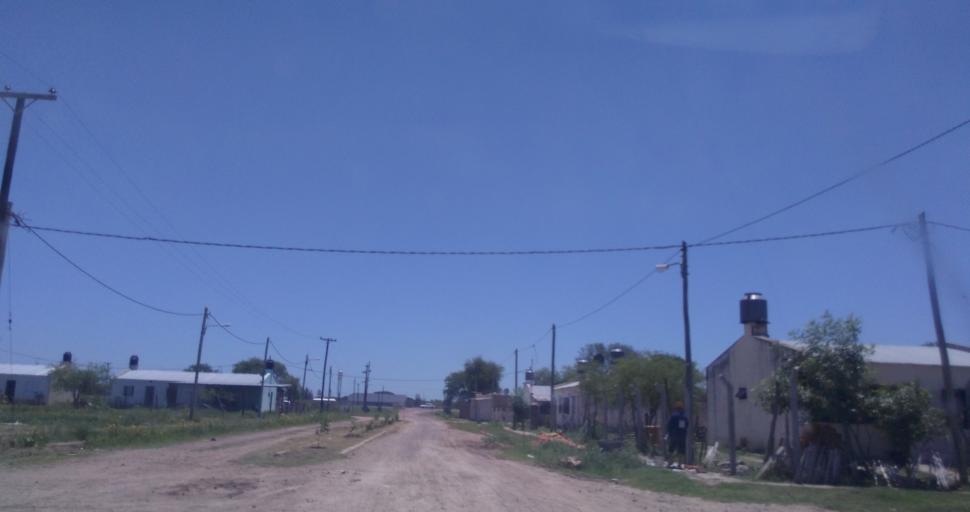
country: AR
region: Chaco
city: Fontana
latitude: -27.4757
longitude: -59.0533
